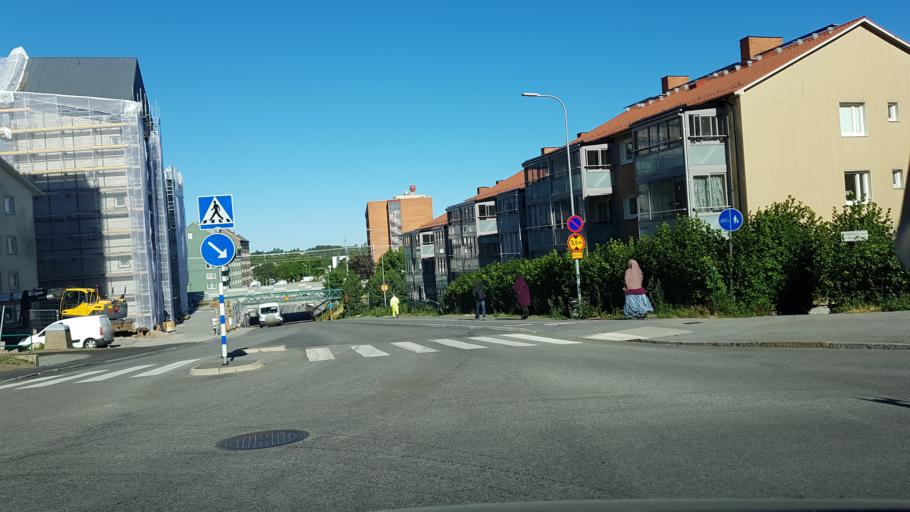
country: SE
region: Stockholm
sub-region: Jarfalla Kommun
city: Jakobsberg
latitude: 59.4178
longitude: 17.8350
